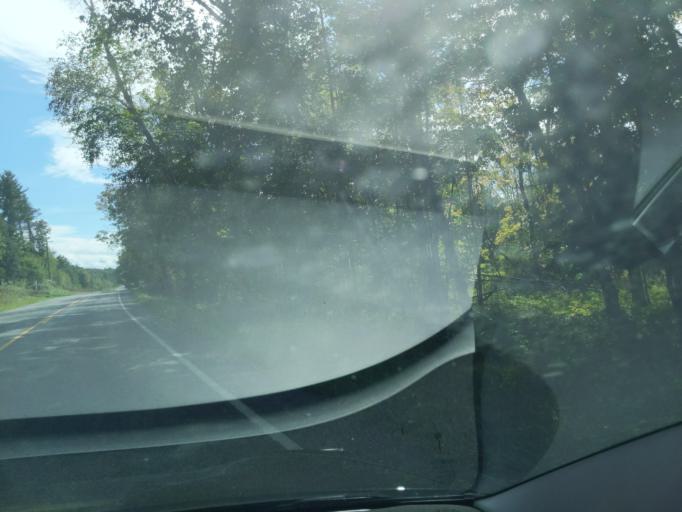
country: US
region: Michigan
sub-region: Antrim County
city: Bellaire
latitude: 45.0198
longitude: -85.2922
